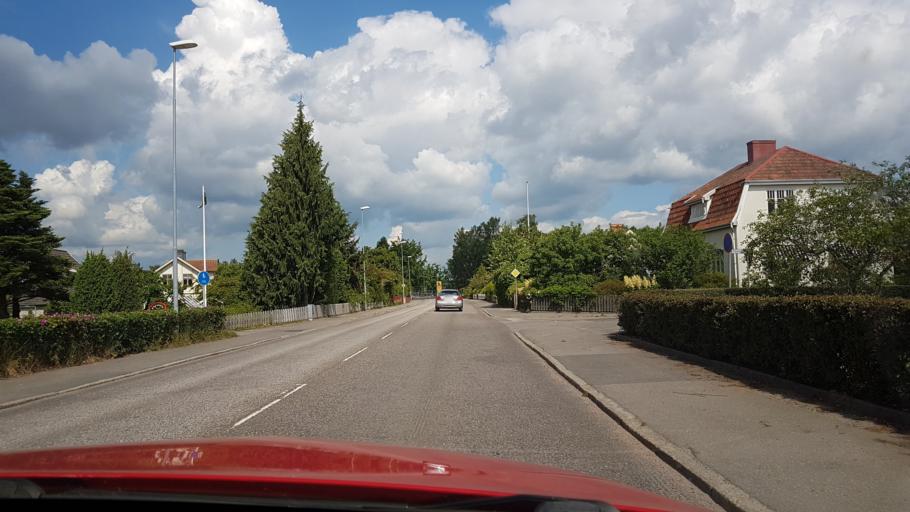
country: SE
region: Vaestra Goetaland
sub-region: Hjo Kommun
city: Hjo
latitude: 58.3099
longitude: 14.2827
